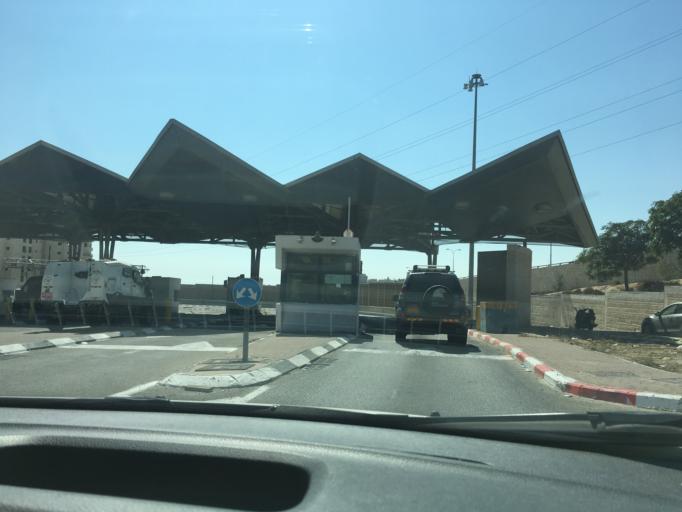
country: PS
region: West Bank
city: `Anata
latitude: 31.8086
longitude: 35.2420
